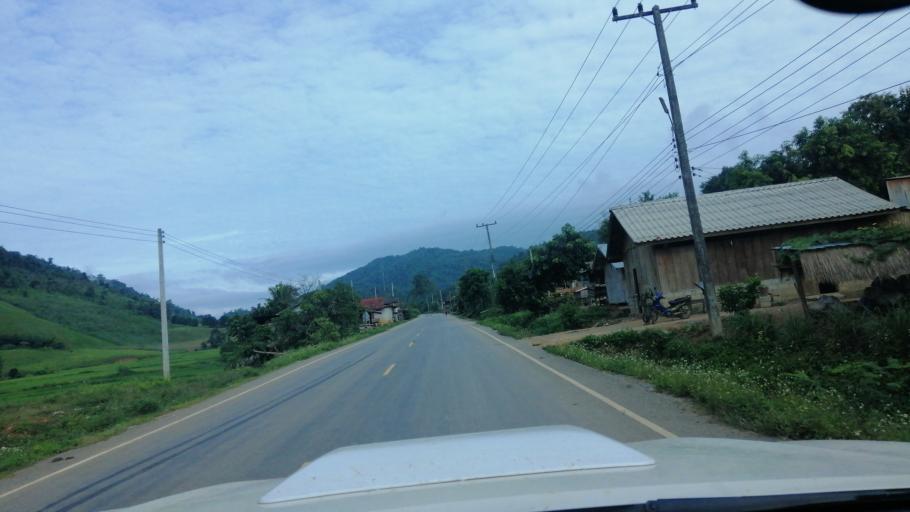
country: TH
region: Phayao
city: Phu Sang
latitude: 19.6675
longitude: 100.4506
